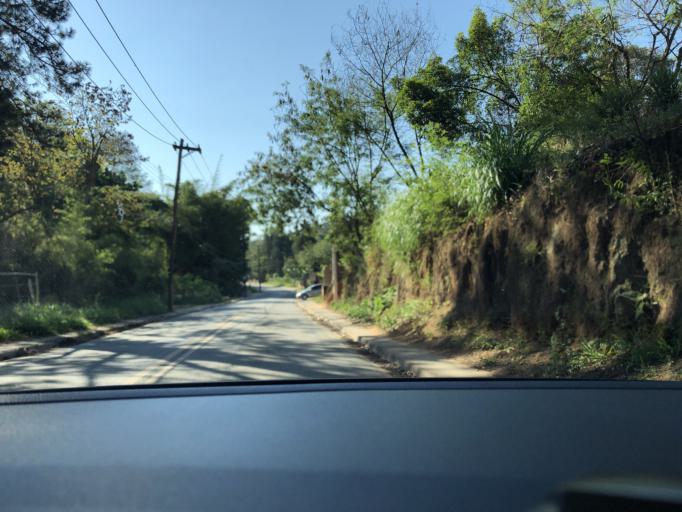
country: BR
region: Sao Paulo
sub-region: Campo Limpo Paulista
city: Campo Limpo Paulista
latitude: -23.1816
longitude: -46.8056
